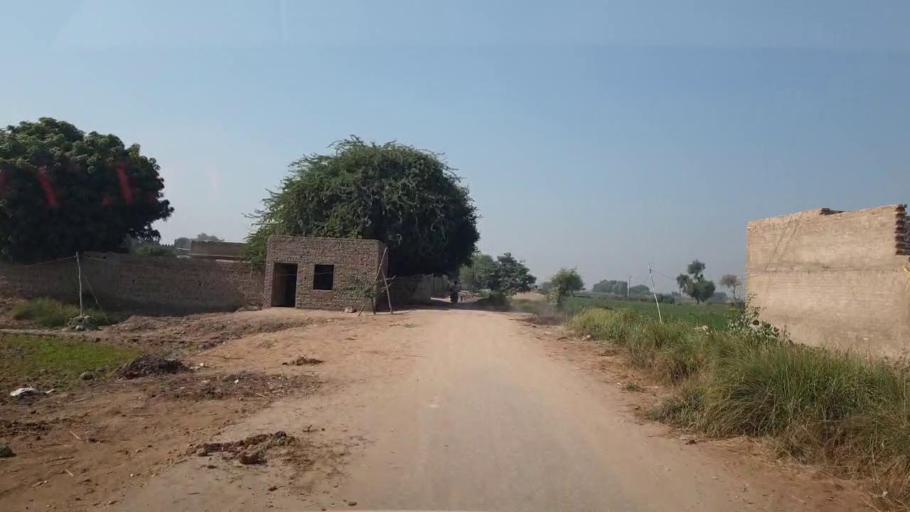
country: PK
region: Sindh
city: Bhan
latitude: 26.6413
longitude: 67.7164
